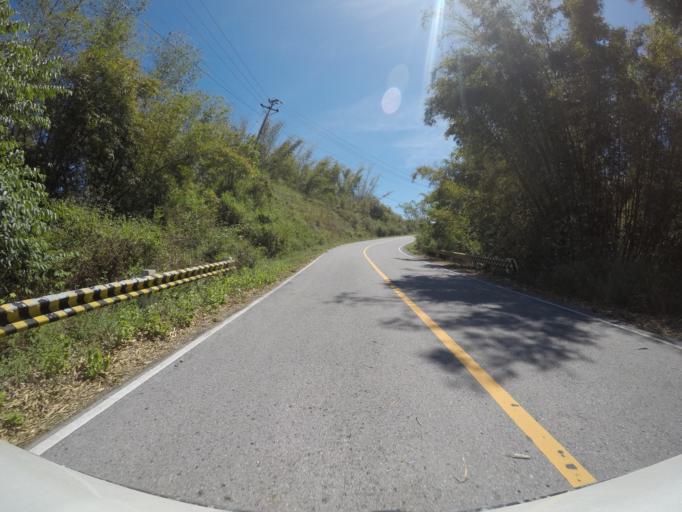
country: TL
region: Manatuto
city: Manatuto
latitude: -8.8775
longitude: 125.9900
